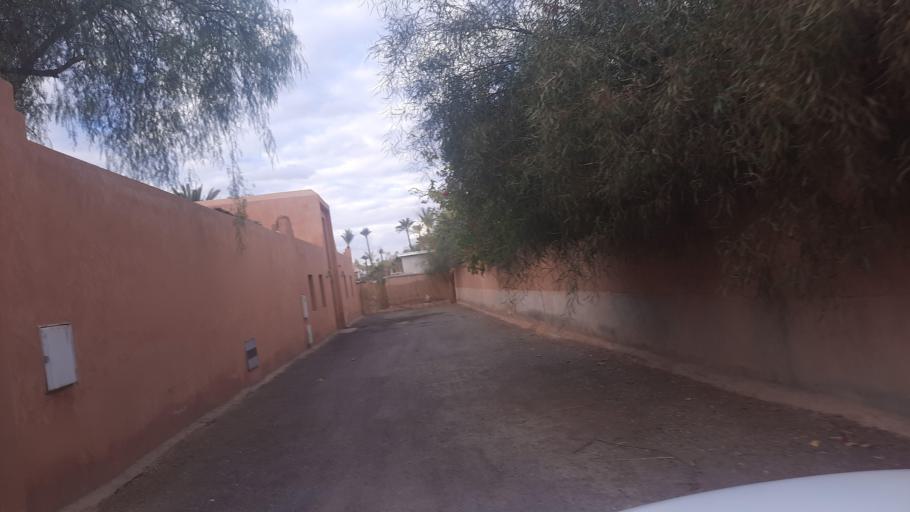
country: MA
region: Marrakech-Tensift-Al Haouz
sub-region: Marrakech
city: Marrakesh
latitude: 31.6781
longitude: -7.9537
